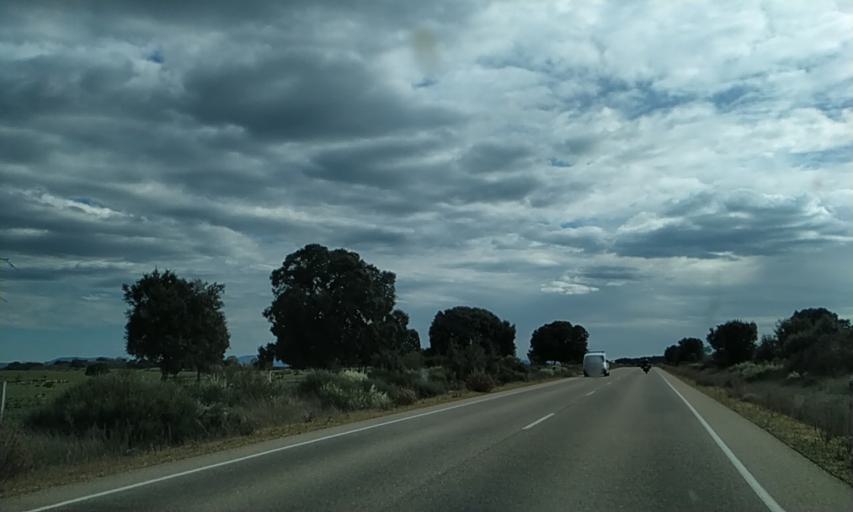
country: ES
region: Castille and Leon
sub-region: Provincia de Salamanca
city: Herguijuela de Ciudad Rodrigo
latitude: 40.4638
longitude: -6.5864
